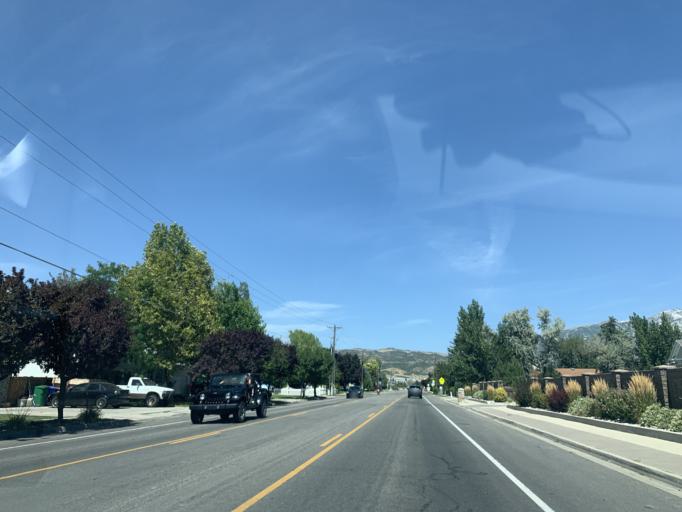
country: US
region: Utah
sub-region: Utah County
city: Lehi
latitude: 40.4164
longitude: -111.8303
